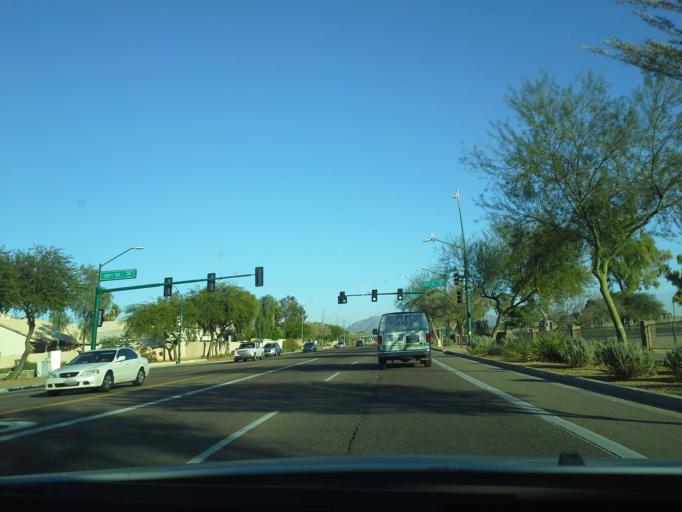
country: US
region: Arizona
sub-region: Maricopa County
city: Paradise Valley
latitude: 33.6551
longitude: -112.0057
